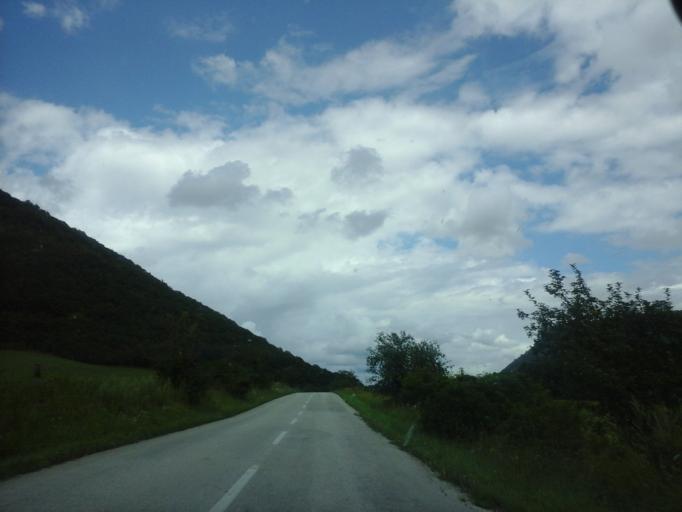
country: SK
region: Kosicky
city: Roznava
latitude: 48.5681
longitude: 20.3933
